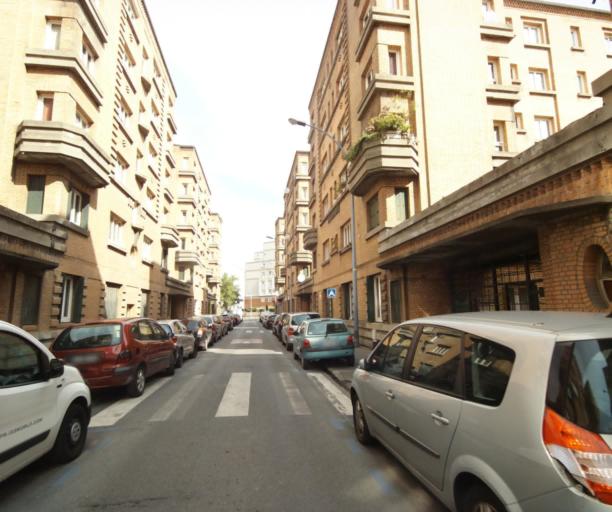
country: FR
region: Ile-de-France
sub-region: Departement du Val-d'Oise
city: Bezons
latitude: 48.9124
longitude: 2.2264
